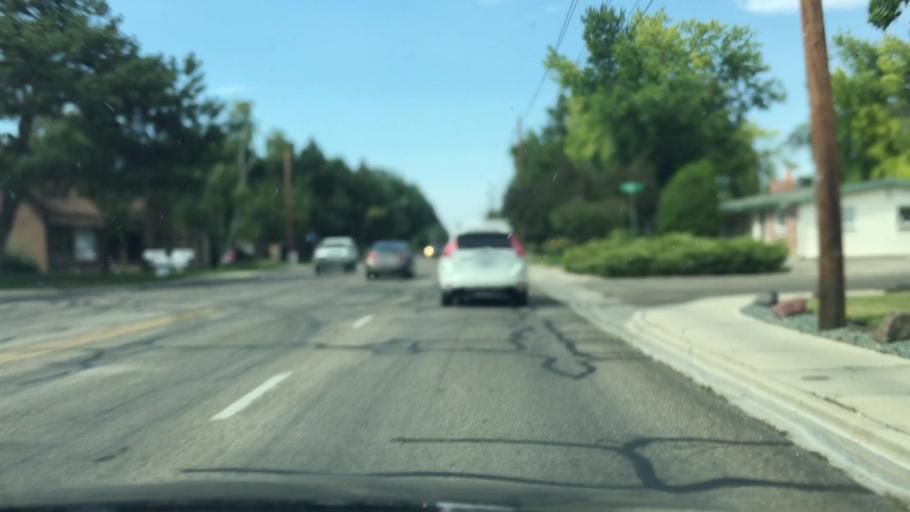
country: US
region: Idaho
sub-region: Ada County
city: Garden City
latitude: 43.6283
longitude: -116.2742
